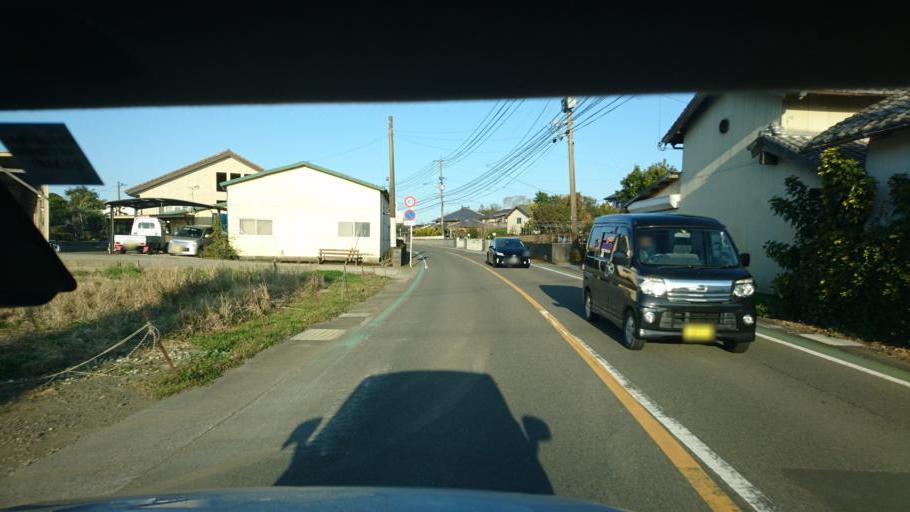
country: JP
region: Miyazaki
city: Miyazaki-shi
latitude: 31.8434
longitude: 131.4063
